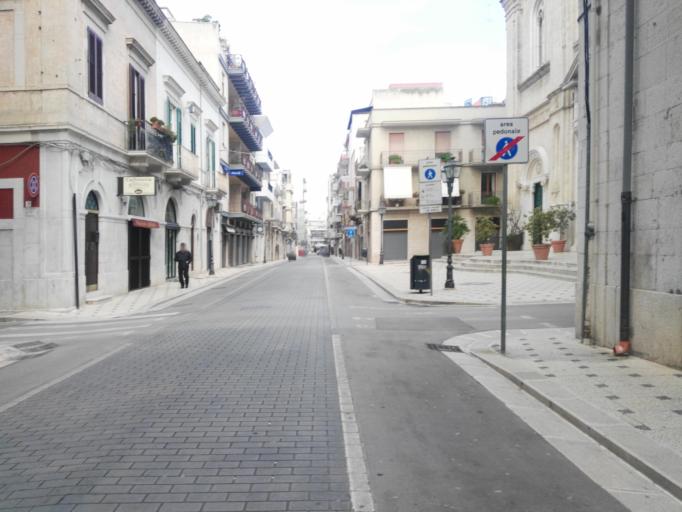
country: IT
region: Apulia
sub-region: Provincia di Barletta - Andria - Trani
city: Andria
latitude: 41.2264
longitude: 16.2999
